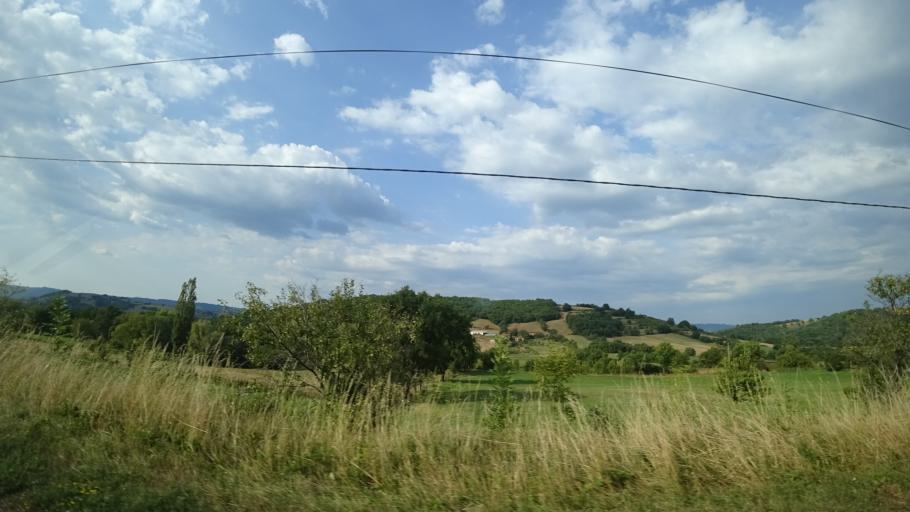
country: FR
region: Midi-Pyrenees
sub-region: Departement de l'Aveyron
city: Saint-Christophe-Vallon
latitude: 44.4986
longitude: 2.3767
